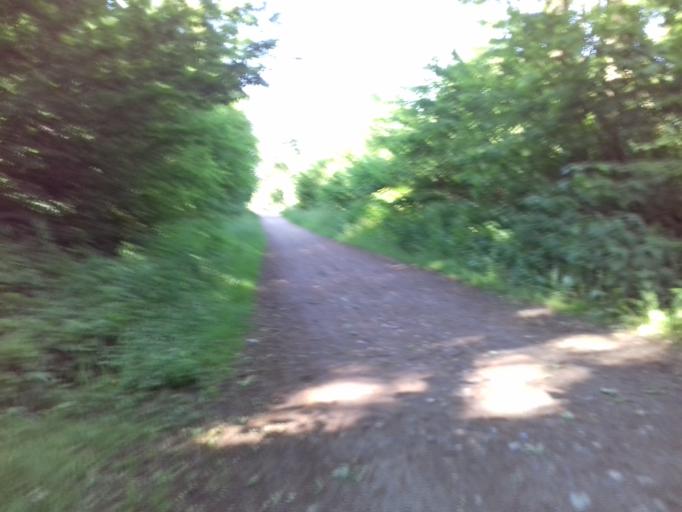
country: DE
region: Schleswig-Holstein
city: Tasdorf
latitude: 54.0852
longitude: 10.0114
